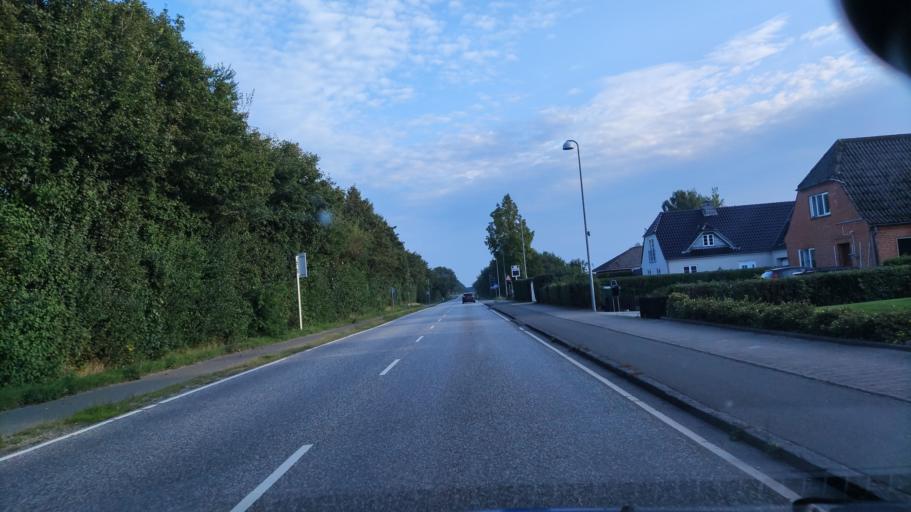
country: DK
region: South Denmark
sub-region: Aabenraa Kommune
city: Tinglev
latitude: 54.9311
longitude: 9.2384
